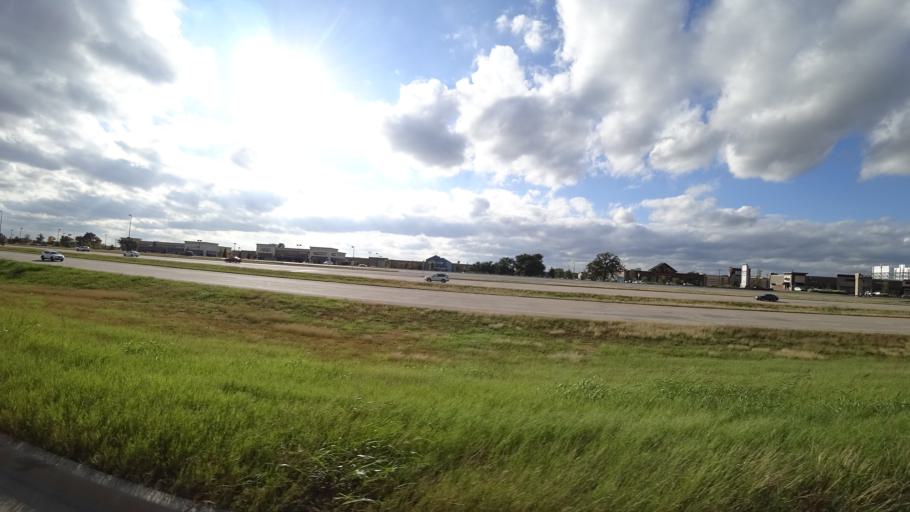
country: US
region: Texas
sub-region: Williamson County
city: Cedar Park
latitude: 30.5300
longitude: -97.8167
